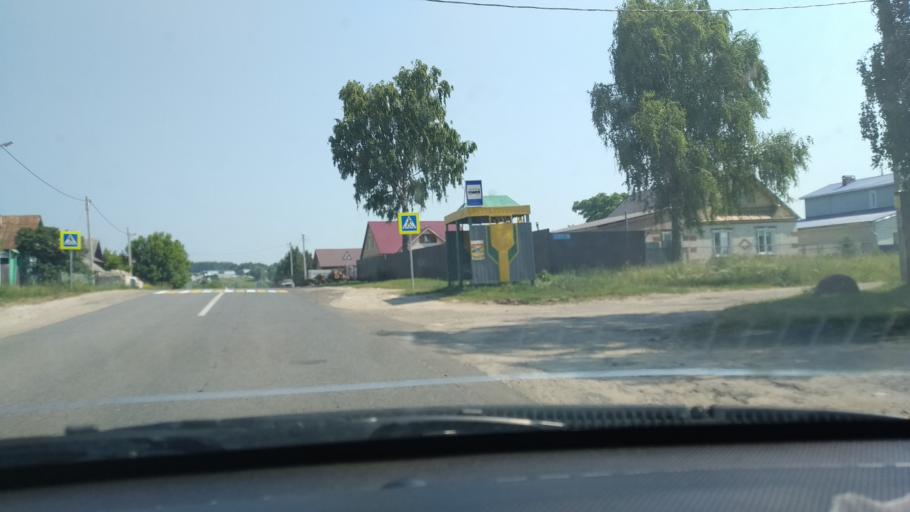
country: RU
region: Tatarstan
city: Osinovo
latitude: 55.9818
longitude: 48.7926
